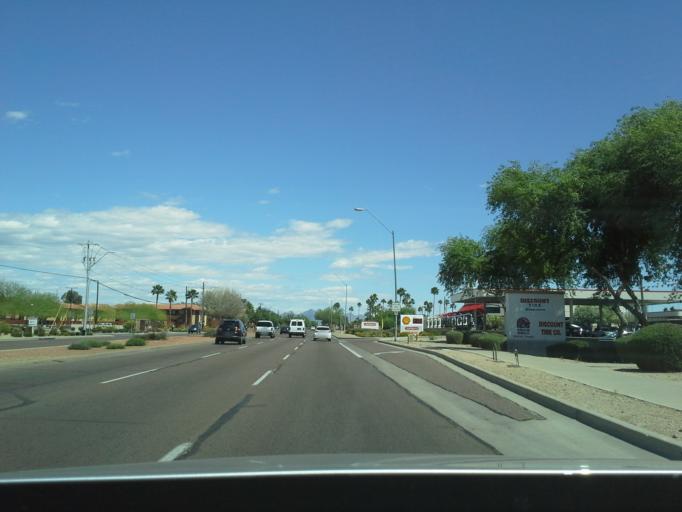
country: US
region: Arizona
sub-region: Maricopa County
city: Glendale
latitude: 33.6401
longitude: -112.0806
